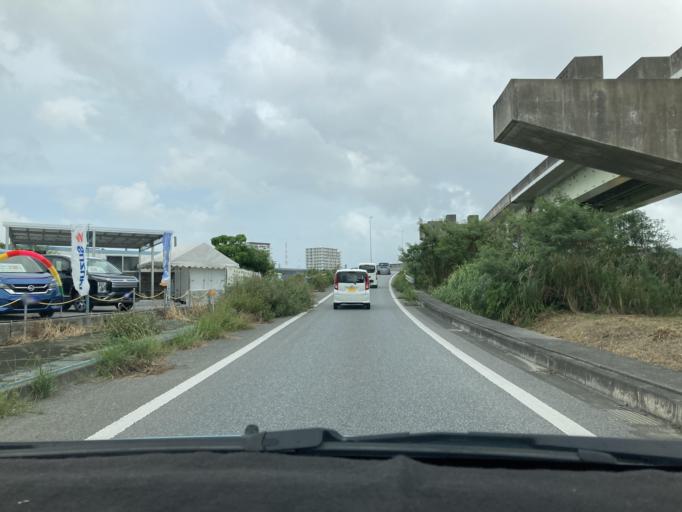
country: JP
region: Okinawa
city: Tomigusuku
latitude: 26.1759
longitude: 127.6690
